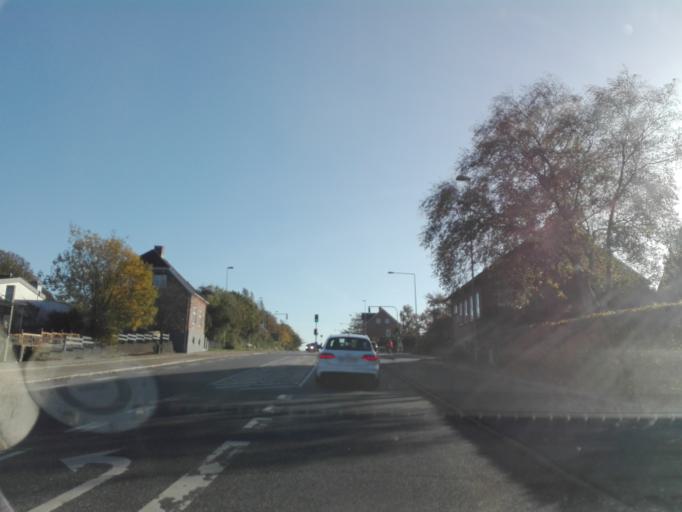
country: DK
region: Central Jutland
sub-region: Arhus Kommune
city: Beder
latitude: 56.1034
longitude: 10.2070
